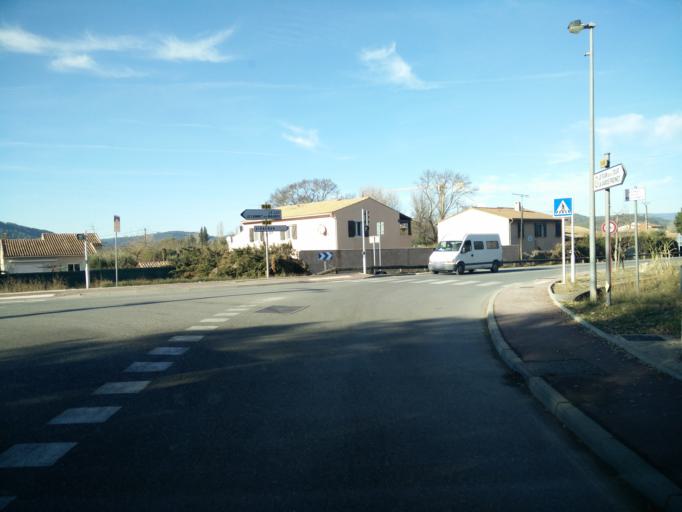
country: FR
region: Provence-Alpes-Cote d'Azur
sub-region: Departement du Var
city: Vidauban
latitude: 43.4158
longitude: 6.4275
